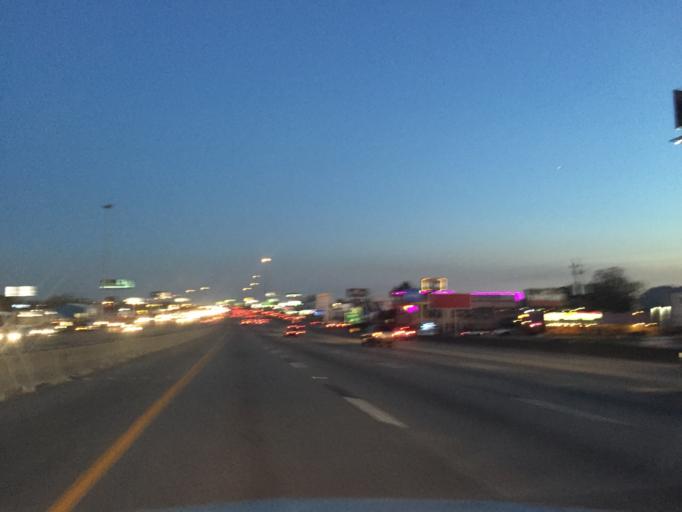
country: US
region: Texas
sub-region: Harris County
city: South Houston
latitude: 29.6512
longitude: -95.2506
